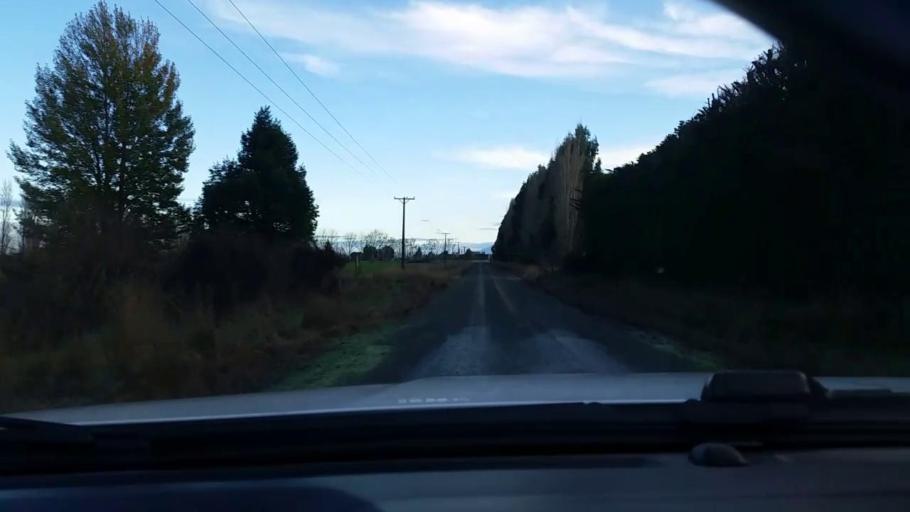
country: NZ
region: Southland
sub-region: Southland District
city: Winton
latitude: -46.1493
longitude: 168.2549
